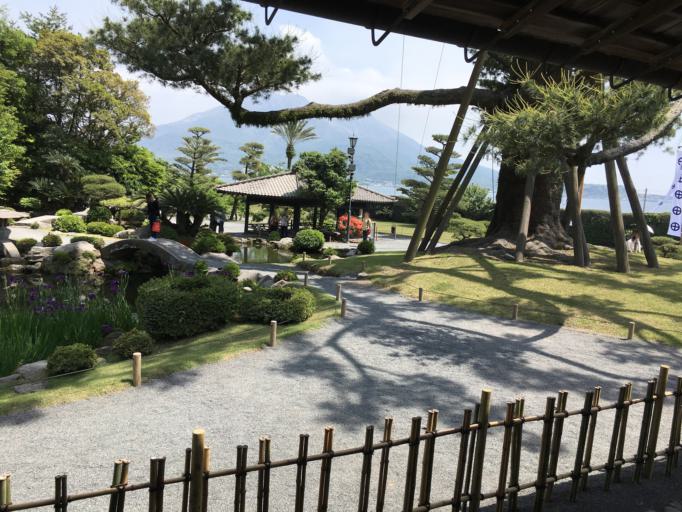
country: JP
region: Kagoshima
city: Kagoshima-shi
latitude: 31.6187
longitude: 130.5805
